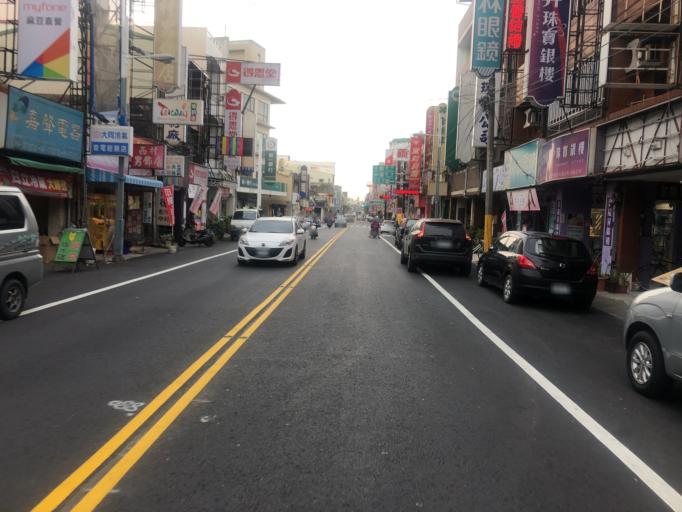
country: TW
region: Taiwan
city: Xinying
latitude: 23.1837
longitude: 120.2498
